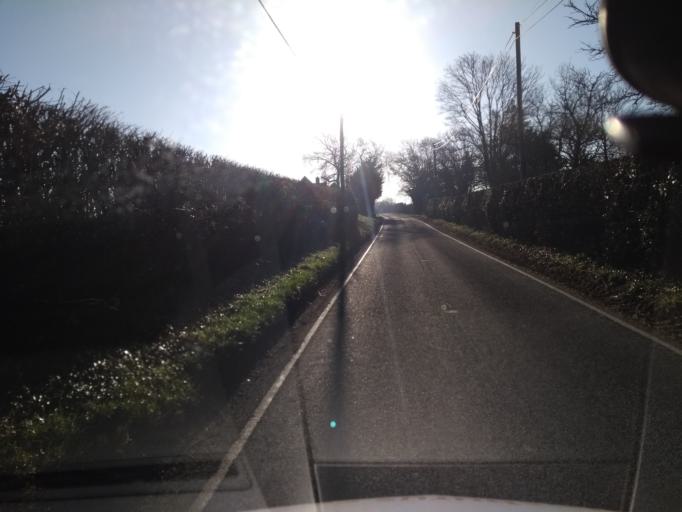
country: GB
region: England
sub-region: Somerset
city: Redlynch
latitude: 51.1030
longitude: -2.4323
